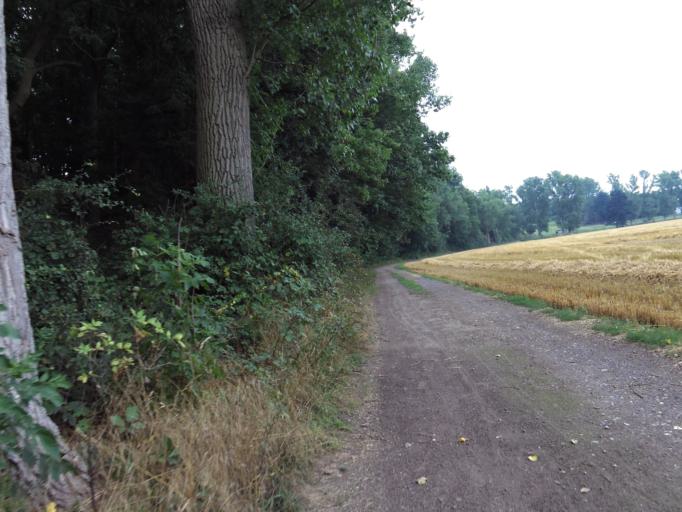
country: DE
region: North Rhine-Westphalia
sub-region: Regierungsbezirk Koln
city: Linnich
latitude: 50.9663
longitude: 6.2580
